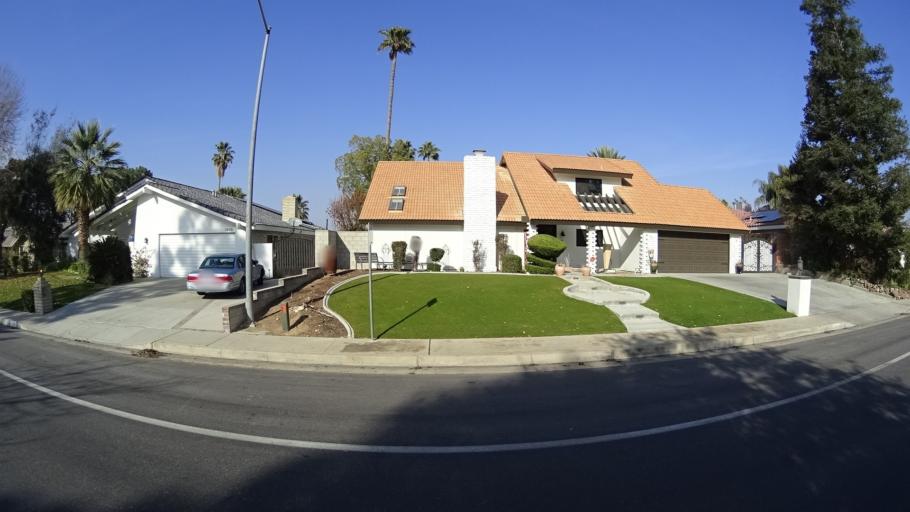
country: US
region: California
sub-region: Kern County
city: Oildale
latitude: 35.4114
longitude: -118.9505
